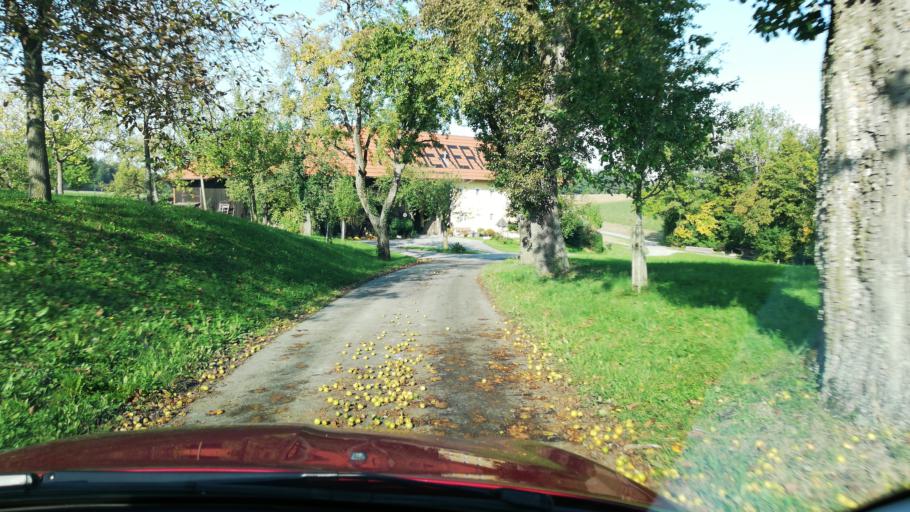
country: AT
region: Upper Austria
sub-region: Politischer Bezirk Kirchdorf an der Krems
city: Kremsmunster
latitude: 48.0954
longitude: 14.1639
